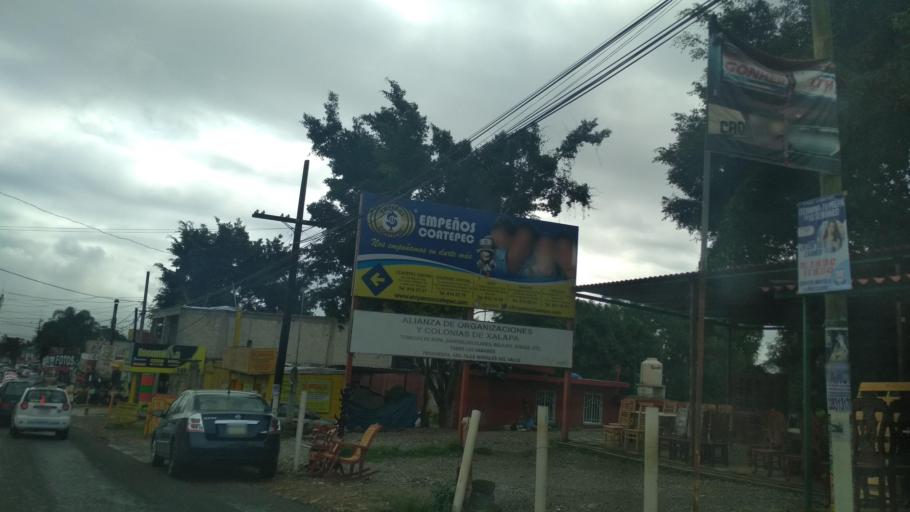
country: MX
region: Veracruz
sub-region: Emiliano Zapata
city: Las Trancas
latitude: 19.5069
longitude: -96.8671
